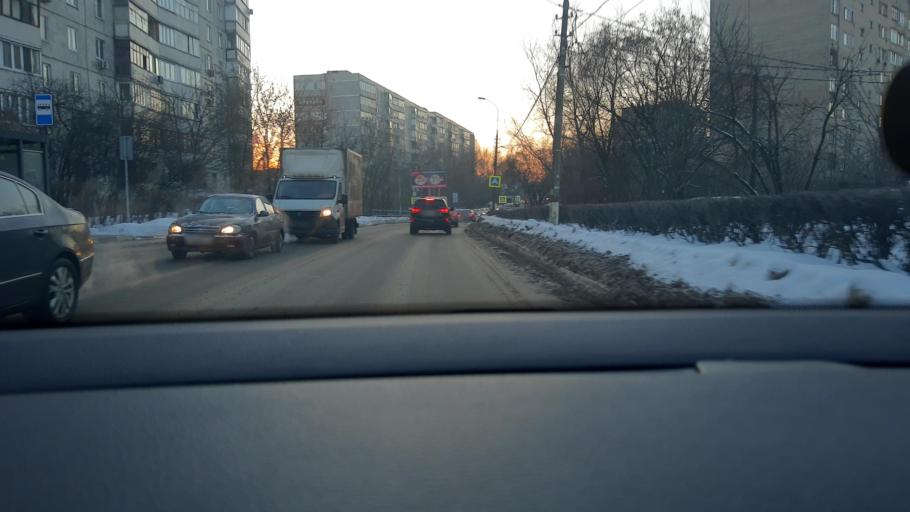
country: RU
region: Moskovskaya
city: Ivanteyevka
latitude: 55.9647
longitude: 37.9173
